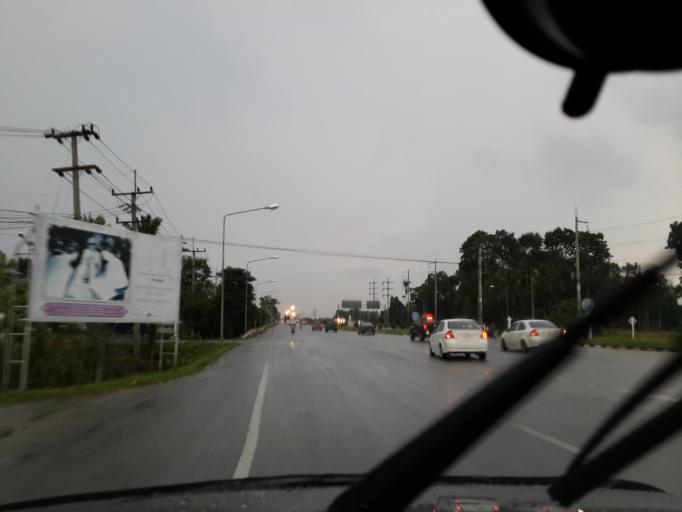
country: TH
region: Yala
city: Yala
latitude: 6.5531
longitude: 101.2630
